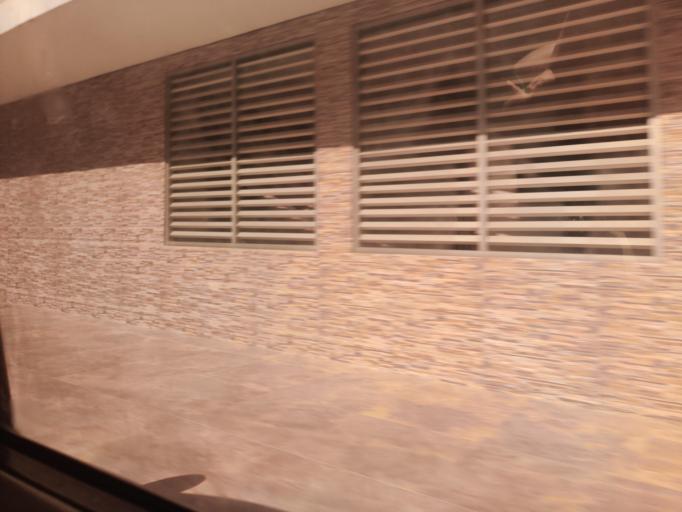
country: CO
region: Atlantico
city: Puerto Colombia
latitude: 10.9982
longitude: -74.9522
